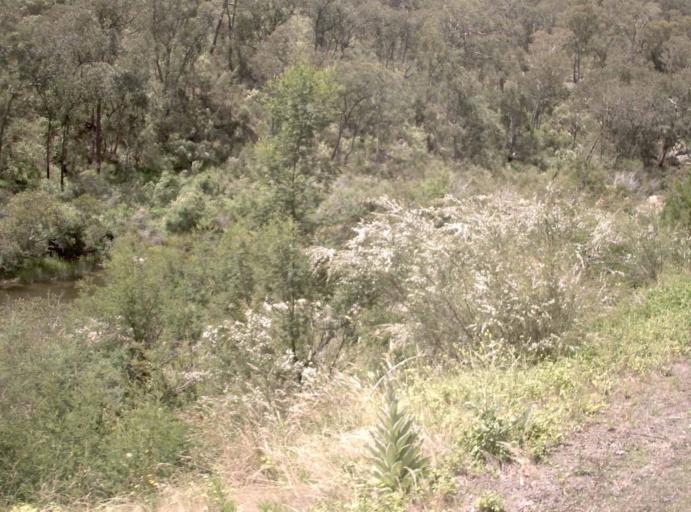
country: AU
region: Victoria
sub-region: East Gippsland
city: Bairnsdale
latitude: -37.4895
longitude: 147.8335
